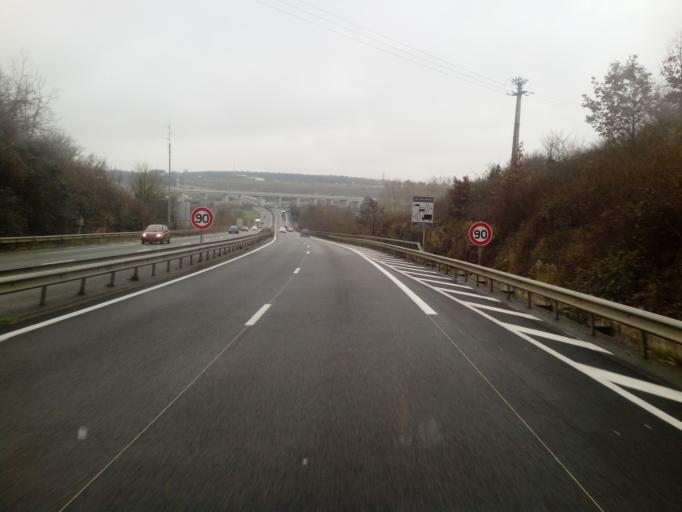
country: FR
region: Poitou-Charentes
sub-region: Departement de la Vienne
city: Chasseneuil-du-Poitou
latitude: 46.6169
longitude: 0.3613
